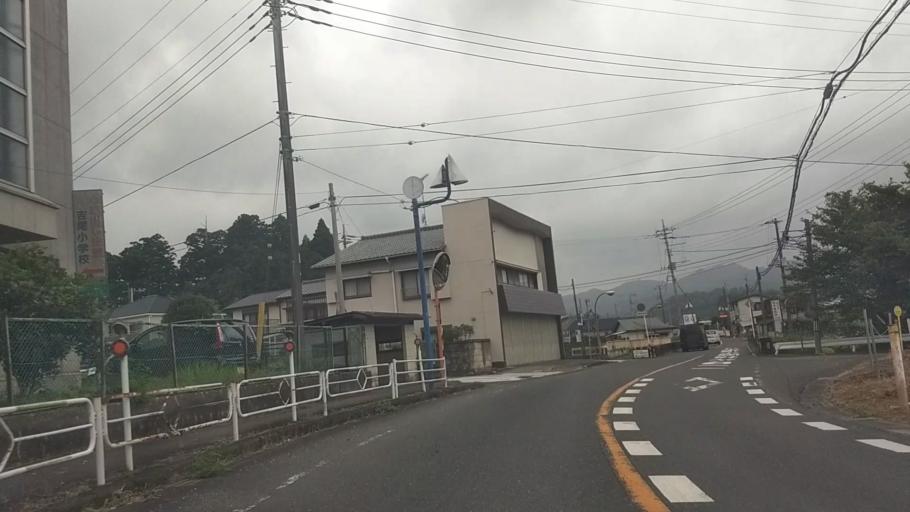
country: JP
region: Chiba
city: Kawaguchi
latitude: 35.1326
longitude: 140.0075
